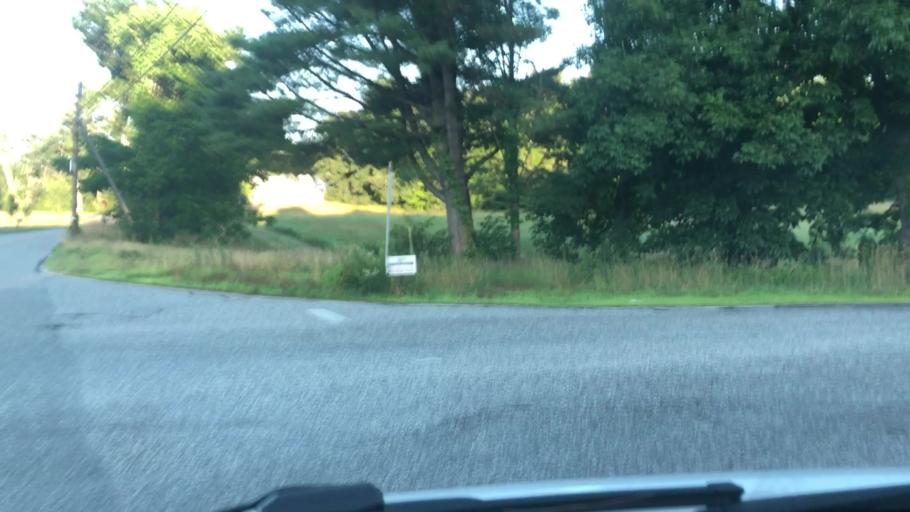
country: US
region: Massachusetts
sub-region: Hampshire County
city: Easthampton
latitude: 42.2382
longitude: -72.6913
